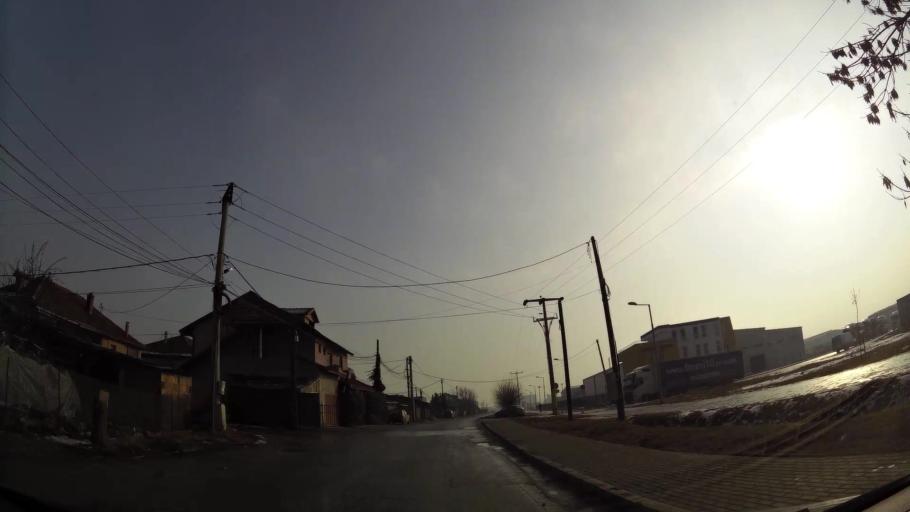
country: MK
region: Ilinden
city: Marino
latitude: 41.9813
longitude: 21.5925
